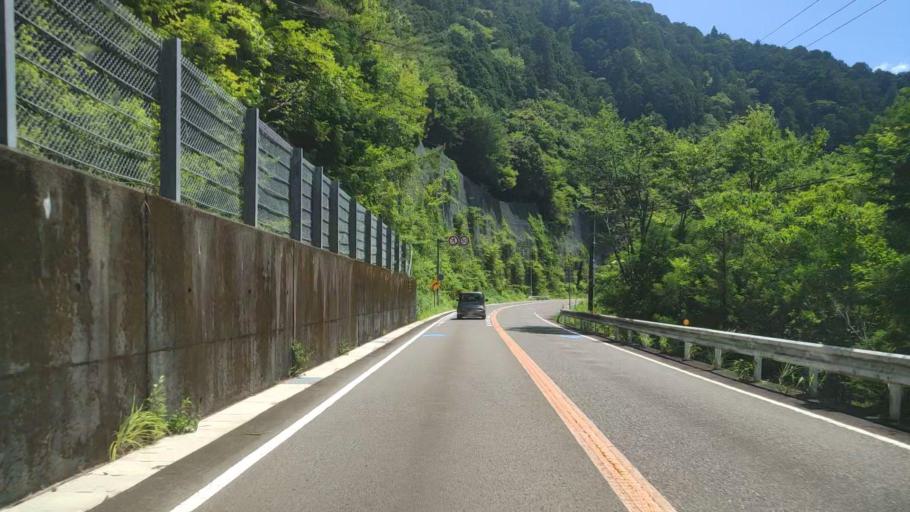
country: JP
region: Mie
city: Owase
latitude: 33.9884
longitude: 136.1122
